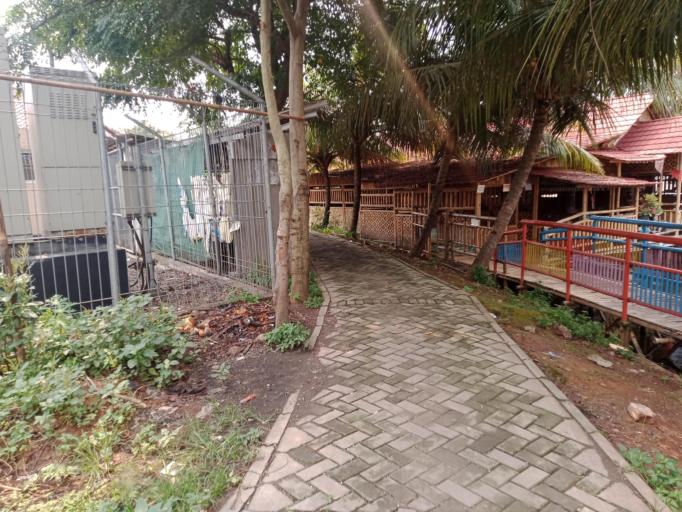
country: ID
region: West Java
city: Pasarkemis
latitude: -6.1978
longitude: 106.5257
